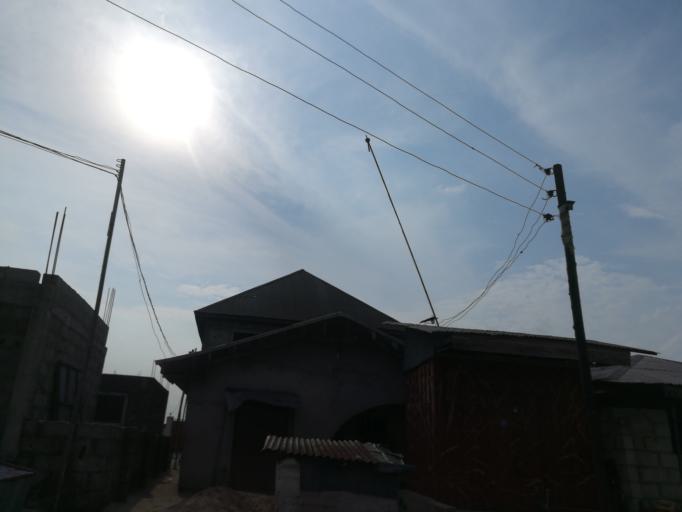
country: NG
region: Rivers
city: Okrika
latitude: 4.7321
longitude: 7.0840
